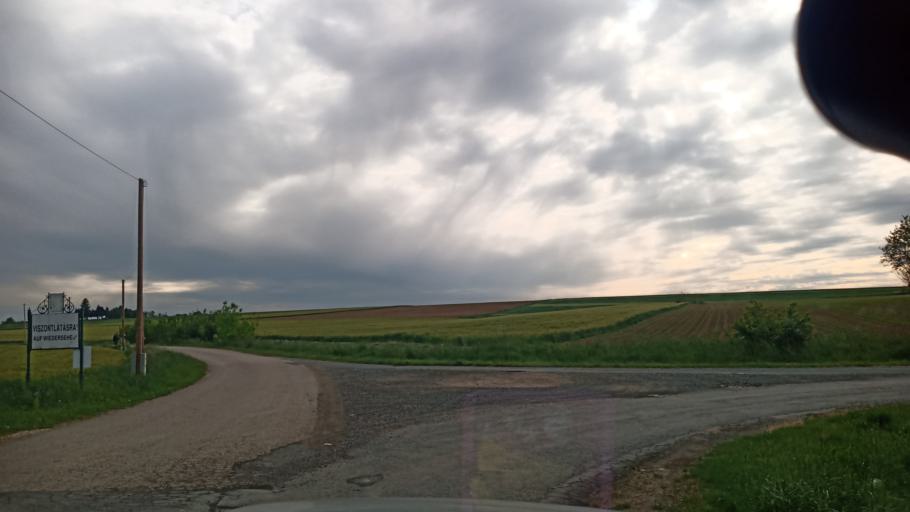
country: HU
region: Zala
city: Pacsa
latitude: 46.7545
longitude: 17.0230
